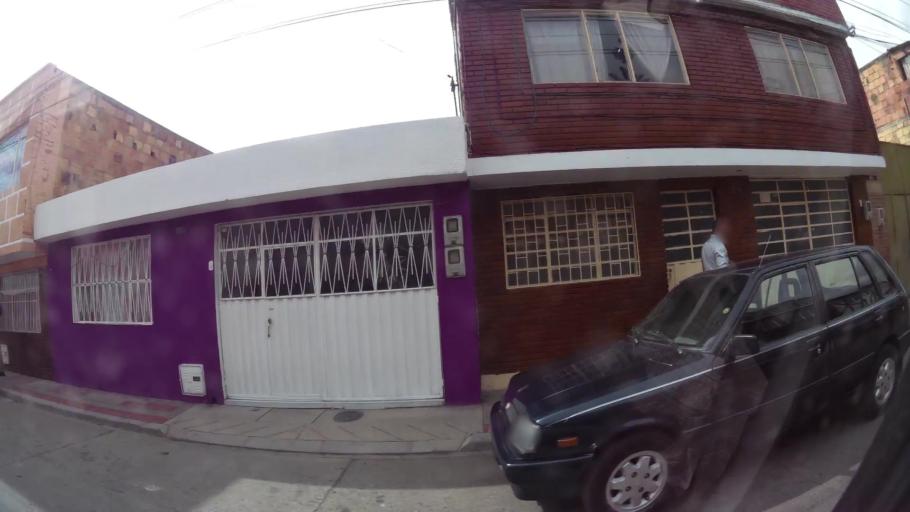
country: CO
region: Cundinamarca
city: Funza
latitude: 4.7085
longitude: -74.2035
